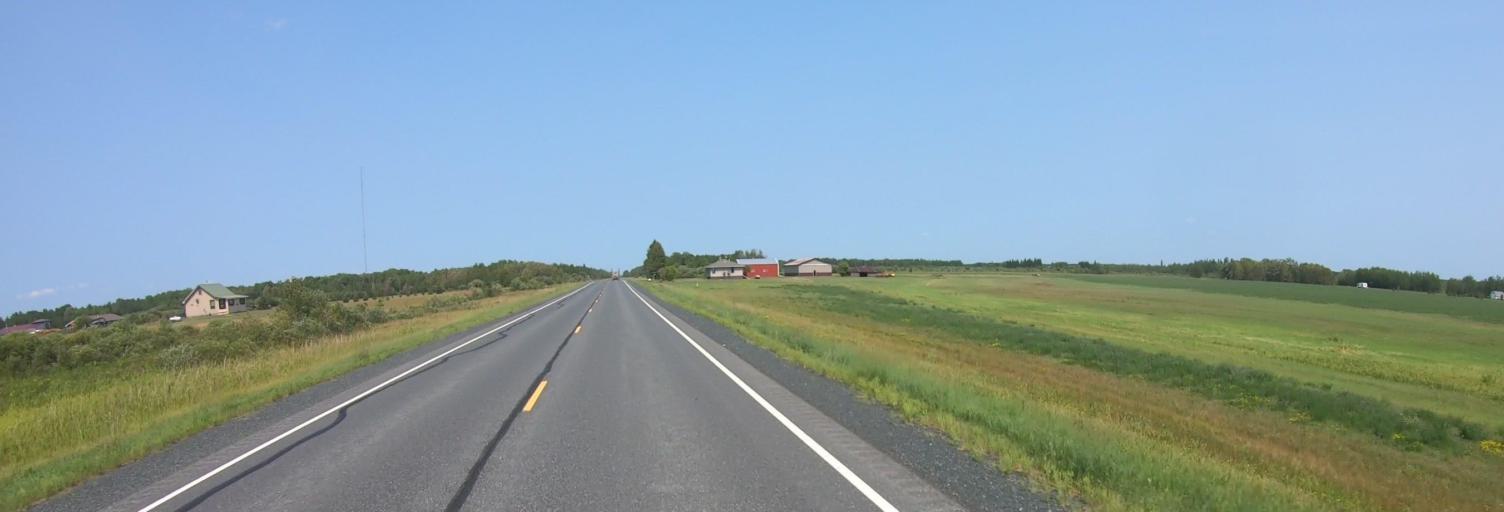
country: US
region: Minnesota
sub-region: Koochiching County
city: International Falls
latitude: 48.5516
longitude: -93.8183
